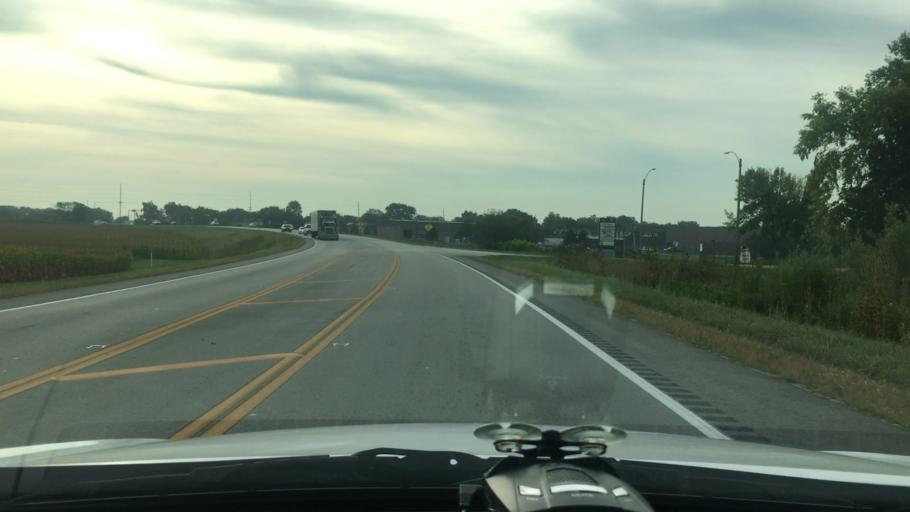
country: US
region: Illinois
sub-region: Champaign County
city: Champaign
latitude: 40.1398
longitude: -88.2824
